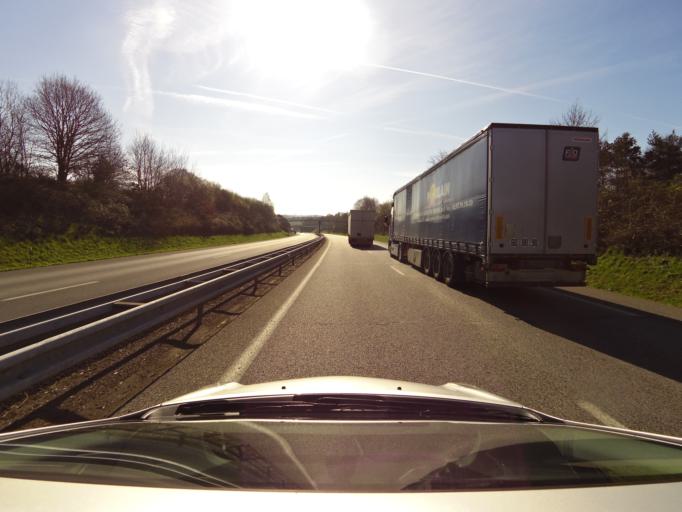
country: FR
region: Brittany
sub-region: Departement du Morbihan
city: Ploermel
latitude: 47.9204
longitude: -2.4083
